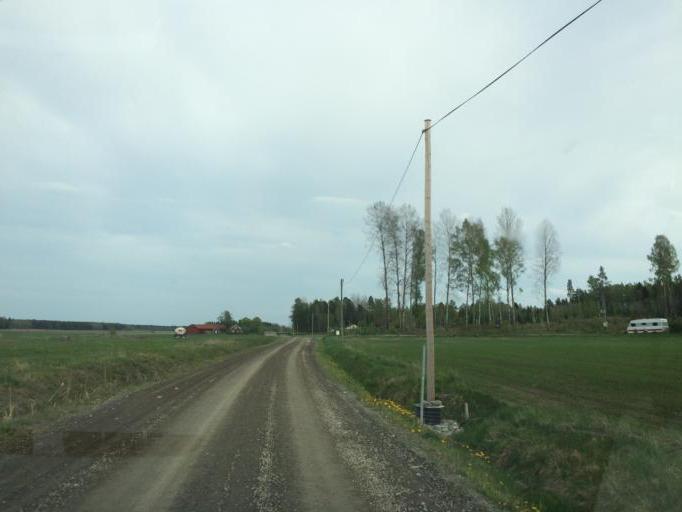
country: SE
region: Vaestmanland
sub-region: Kopings Kommun
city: Koping
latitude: 59.6117
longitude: 16.0514
